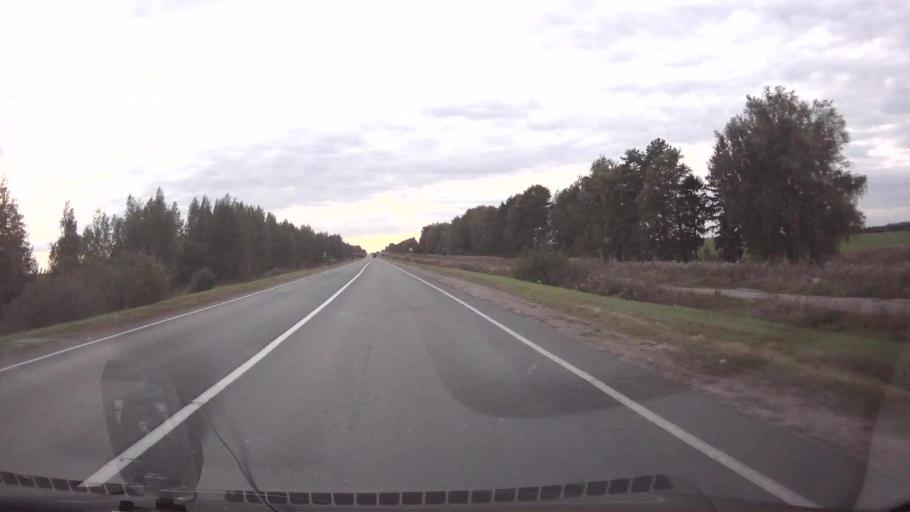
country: RU
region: Mariy-El
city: Sovetskiy
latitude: 56.7474
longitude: 48.3176
